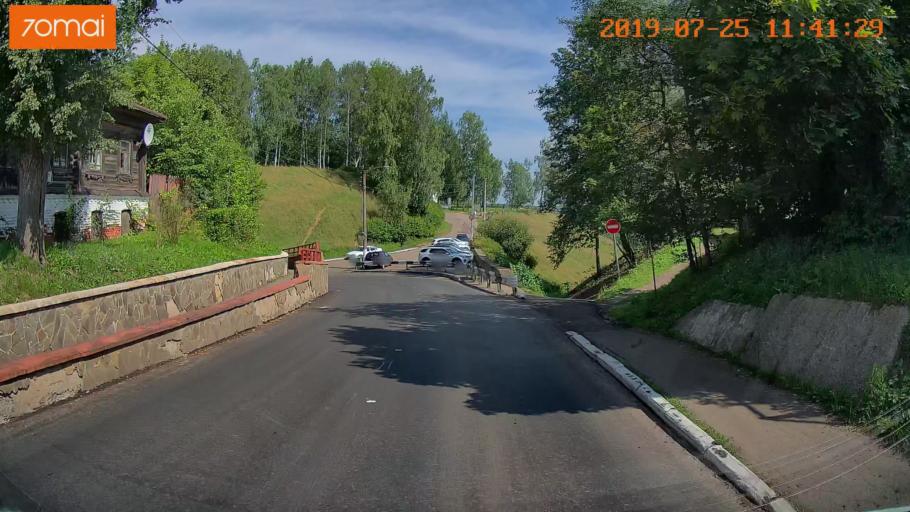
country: RU
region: Ivanovo
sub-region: Privolzhskiy Rayon
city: Ples
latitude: 57.4569
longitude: 41.5139
